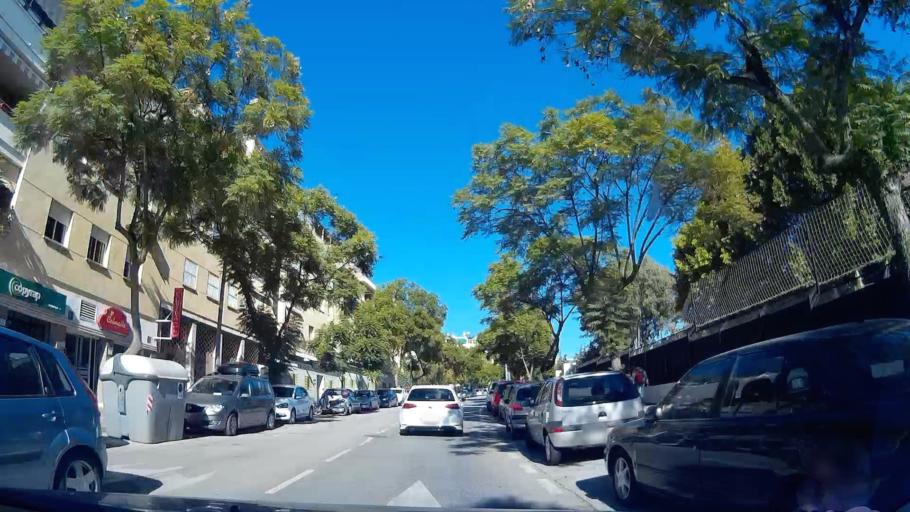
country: ES
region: Andalusia
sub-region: Provincia de Malaga
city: Malaga
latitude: 36.7190
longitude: -4.4759
